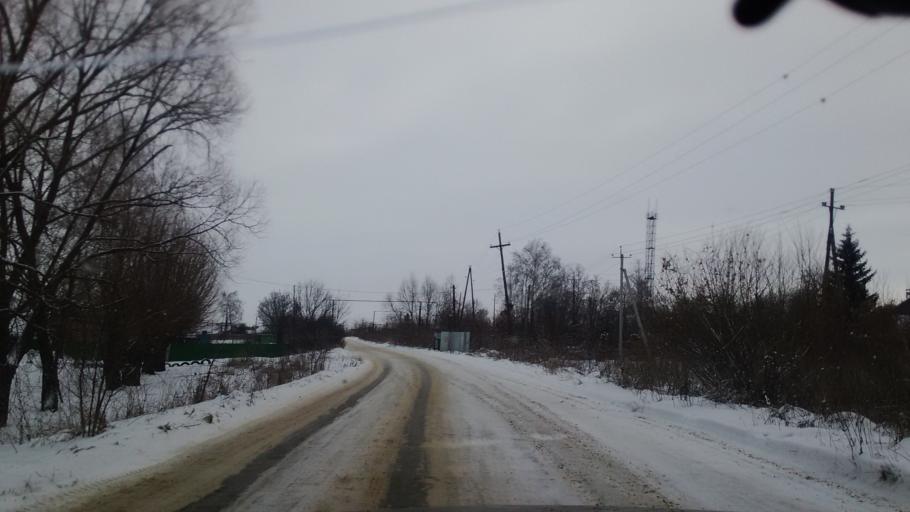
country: RU
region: Tula
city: Bogoroditsk
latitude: 53.7597
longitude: 38.1066
